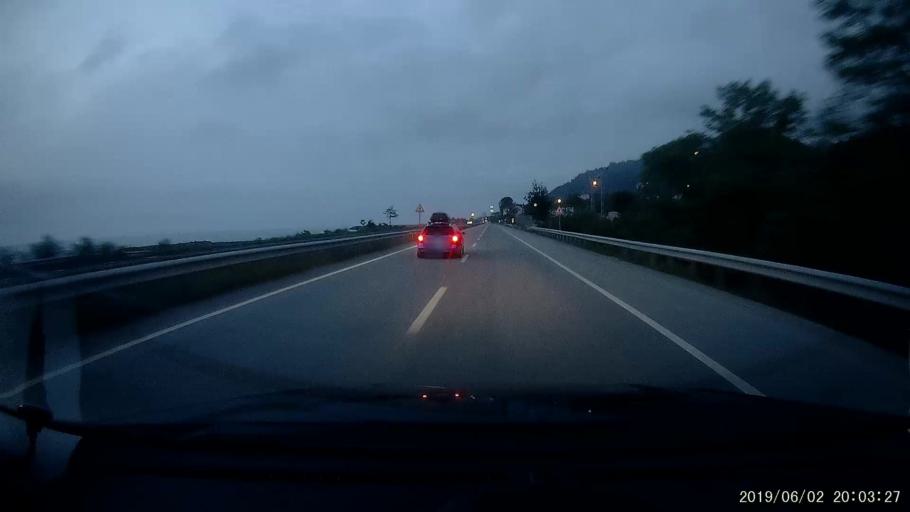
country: TR
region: Giresun
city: Tirebolu
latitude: 41.0212
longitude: 38.8929
